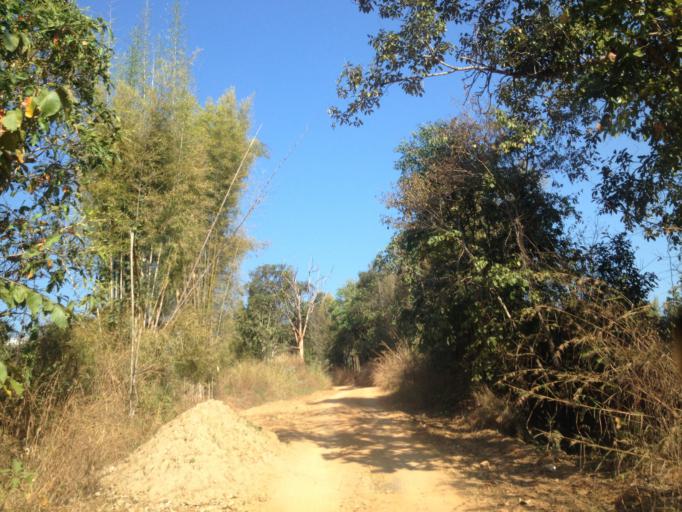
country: TH
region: Mae Hong Son
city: Ban Huai I Huak
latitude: 18.1117
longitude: 98.2085
